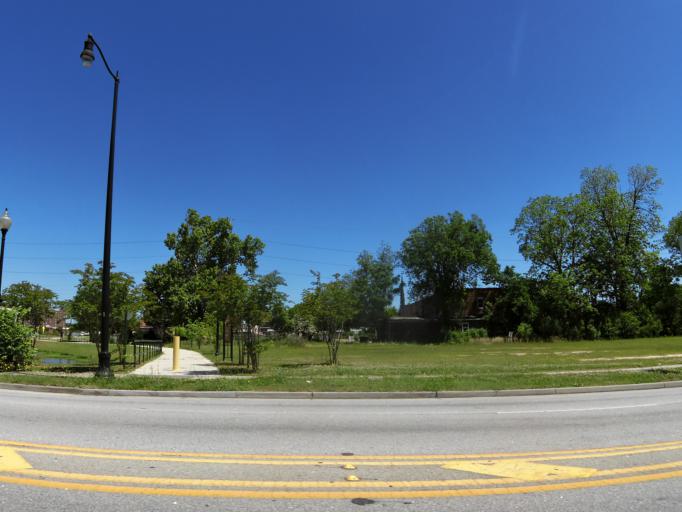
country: US
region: Georgia
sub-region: Richmond County
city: Augusta
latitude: 33.4688
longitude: -81.9703
